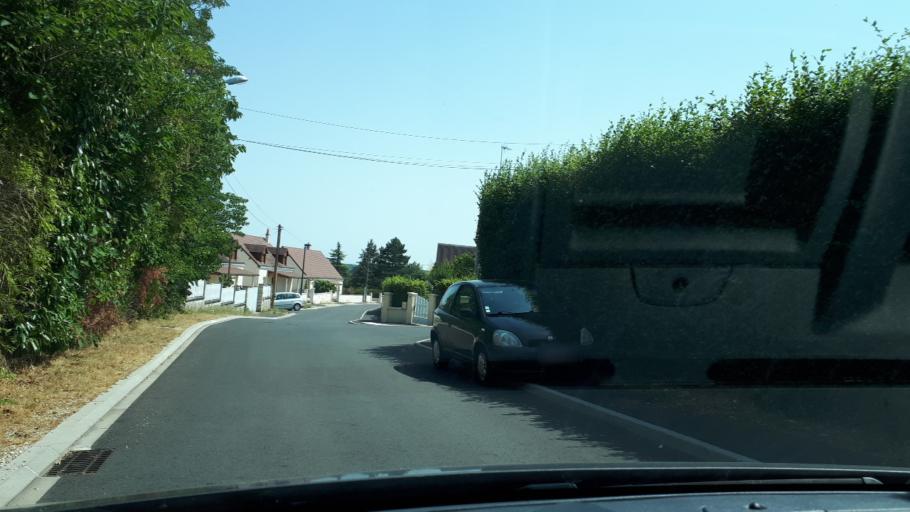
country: FR
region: Centre
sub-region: Departement du Loir-et-Cher
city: Vendome
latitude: 47.8162
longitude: 1.0614
